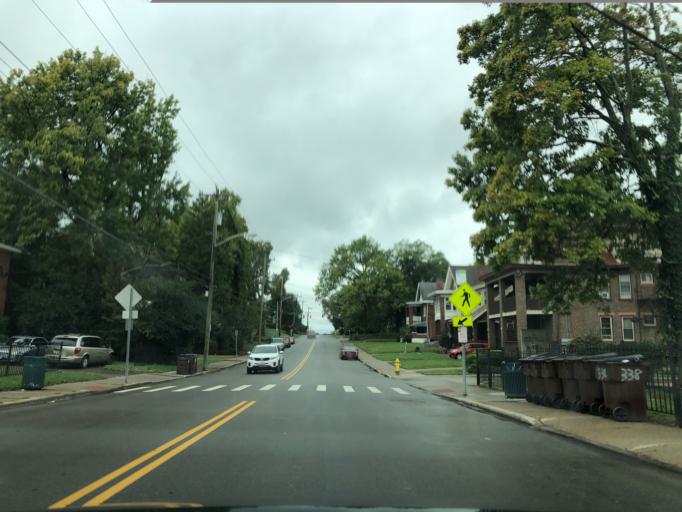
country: US
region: Ohio
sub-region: Hamilton County
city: Saint Bernard
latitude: 39.1463
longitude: -84.5009
